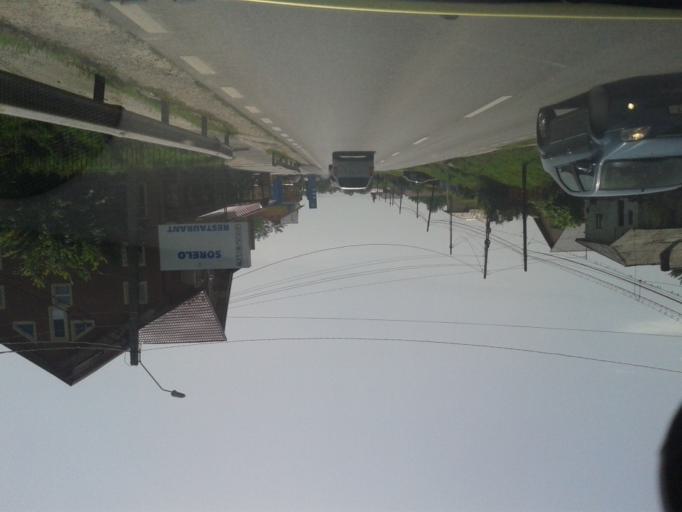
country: RO
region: Arges
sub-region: Comuna Bascov
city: Bascov
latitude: 44.8905
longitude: 24.7584
